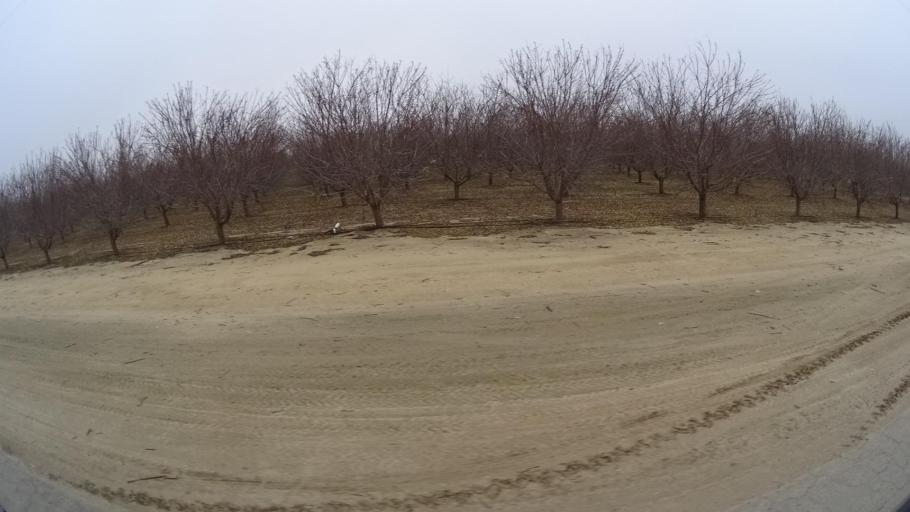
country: US
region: California
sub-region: Kern County
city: Wasco
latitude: 35.5585
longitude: -119.4920
